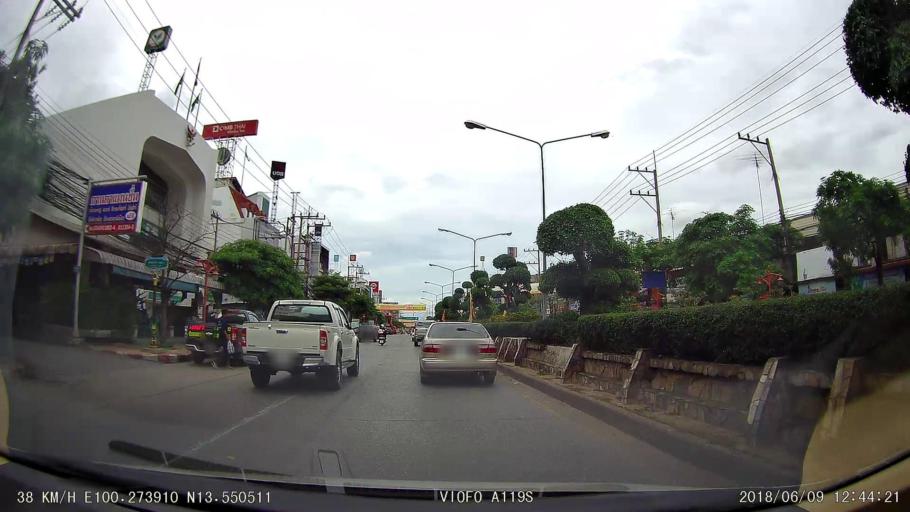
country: TH
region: Samut Sakhon
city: Samut Sakhon
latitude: 13.5527
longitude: 100.2735
